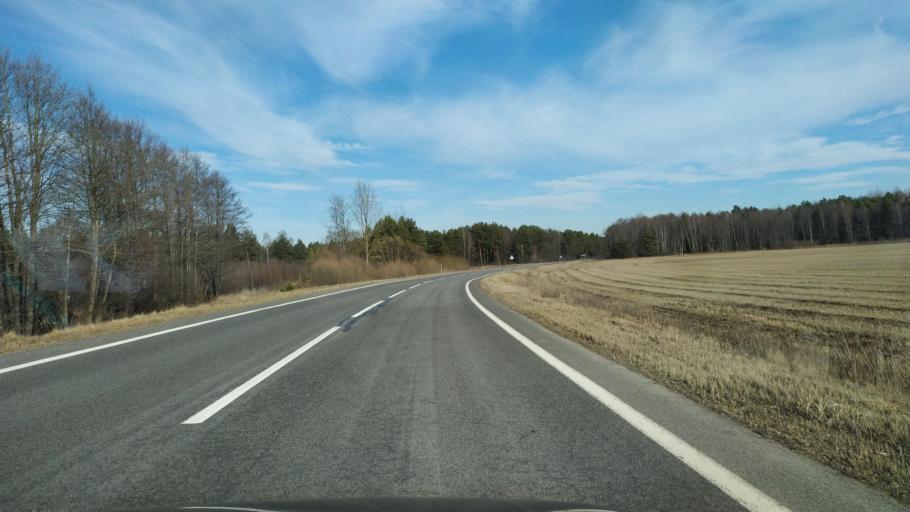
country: BY
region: Brest
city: Zhabinka
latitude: 52.4640
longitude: 24.1445
